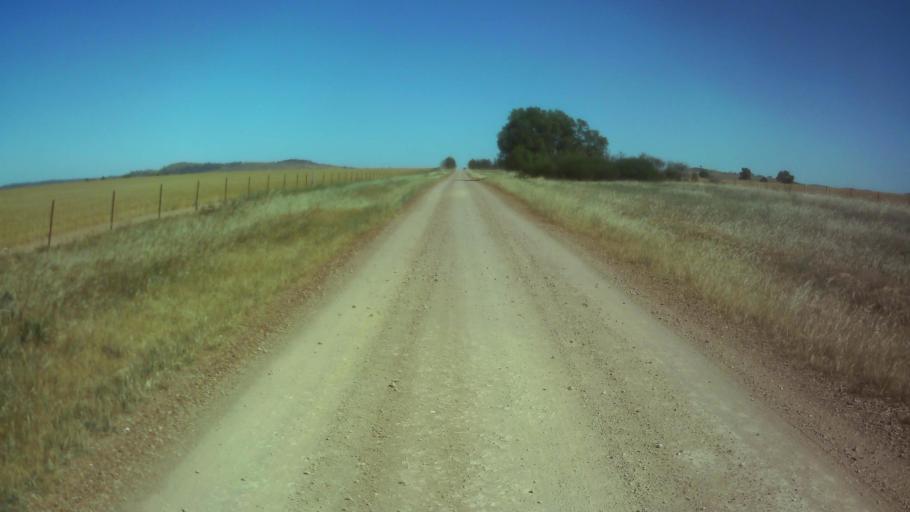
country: AU
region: New South Wales
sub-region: Weddin
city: Grenfell
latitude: -33.9876
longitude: 148.3356
